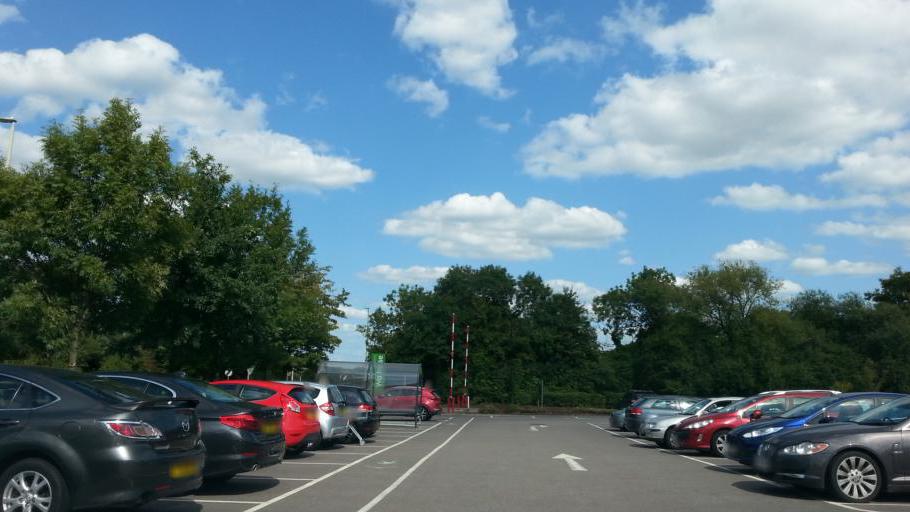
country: GB
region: England
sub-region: Leicestershire
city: Barrow upon Soar
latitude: 52.7372
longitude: -1.1500
